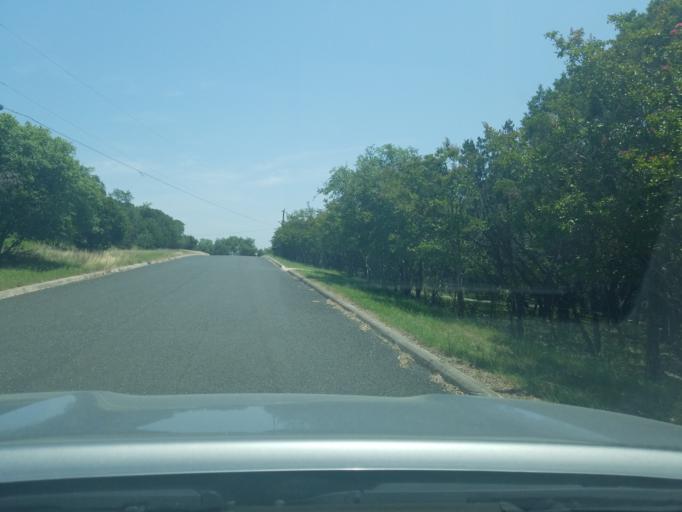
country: US
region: Texas
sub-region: Bexar County
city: Timberwood Park
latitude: 29.6738
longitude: -98.5029
